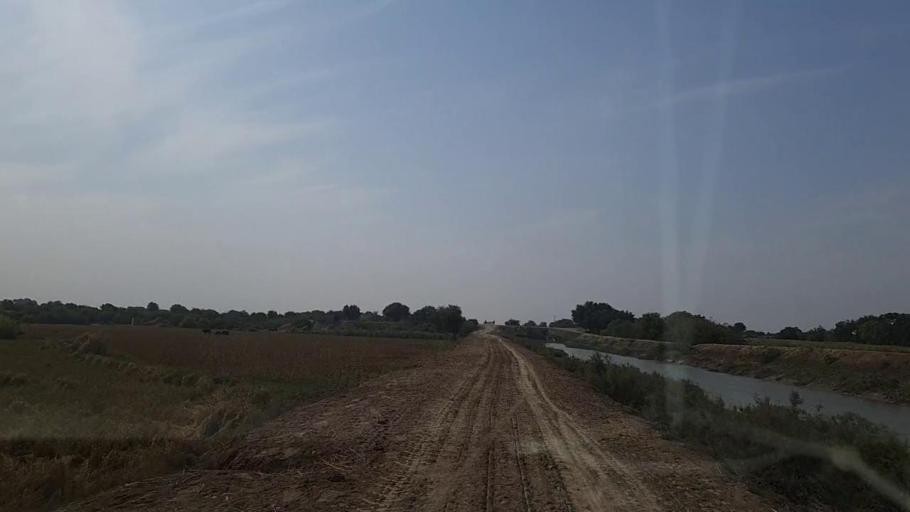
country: PK
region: Sindh
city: Mirpur Batoro
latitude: 24.6418
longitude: 68.2259
